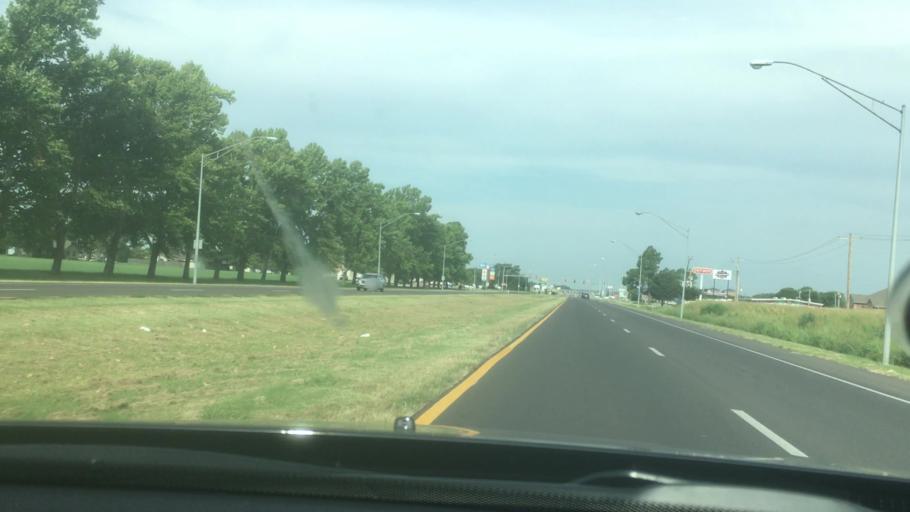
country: US
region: Oklahoma
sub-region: Garvin County
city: Pauls Valley
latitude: 34.7393
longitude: -97.2438
